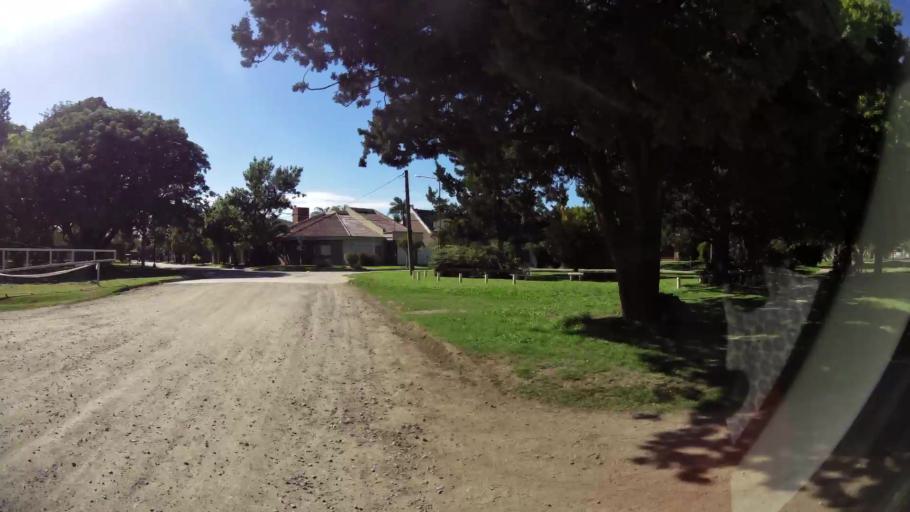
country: AR
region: Santa Fe
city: Esperanza
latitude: -31.4499
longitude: -60.9191
